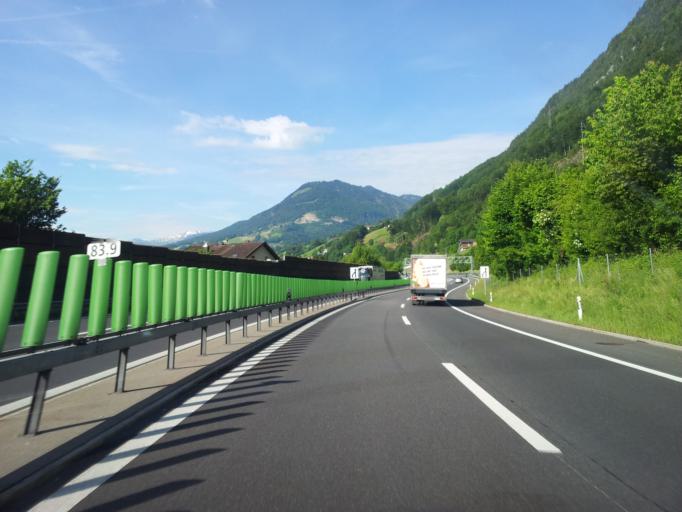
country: CH
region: Obwalden
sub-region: Obwalden
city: Alpnach
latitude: 46.9616
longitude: 8.2882
